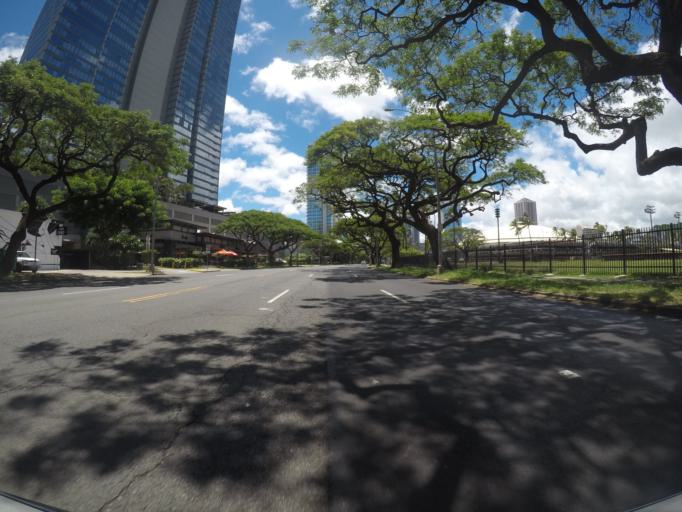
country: US
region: Hawaii
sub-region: Honolulu County
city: Honolulu
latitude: 21.2968
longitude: -157.8506
